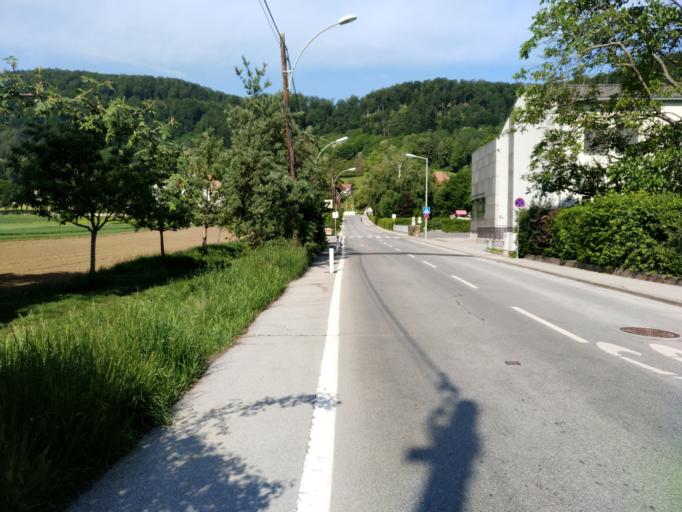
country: AT
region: Styria
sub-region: Graz Stadt
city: Wetzelsdorf
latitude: 47.0466
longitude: 15.3898
